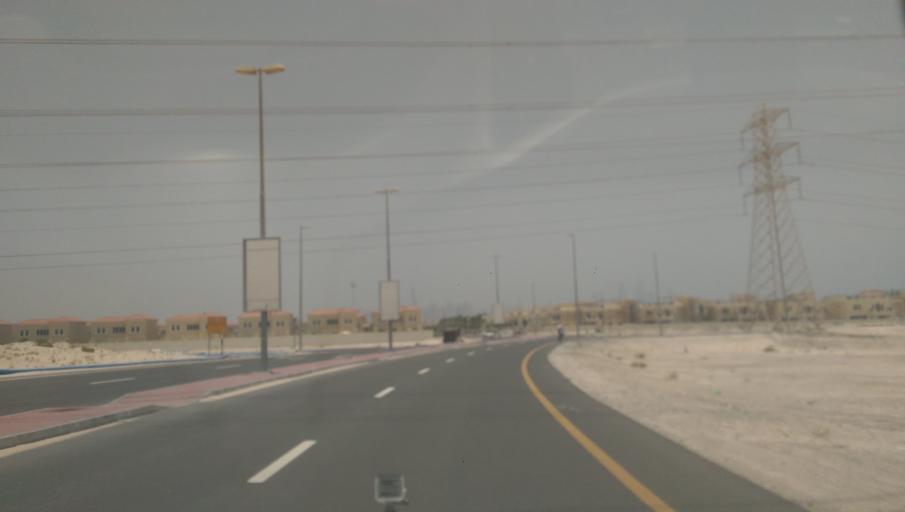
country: AE
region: Dubai
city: Dubai
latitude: 25.0389
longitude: 55.1733
